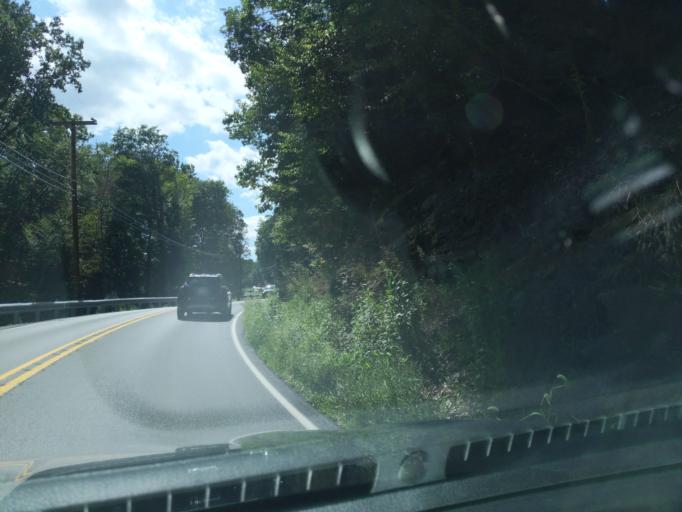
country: US
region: Pennsylvania
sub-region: Blair County
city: Greenwood
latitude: 40.5200
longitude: -78.3050
